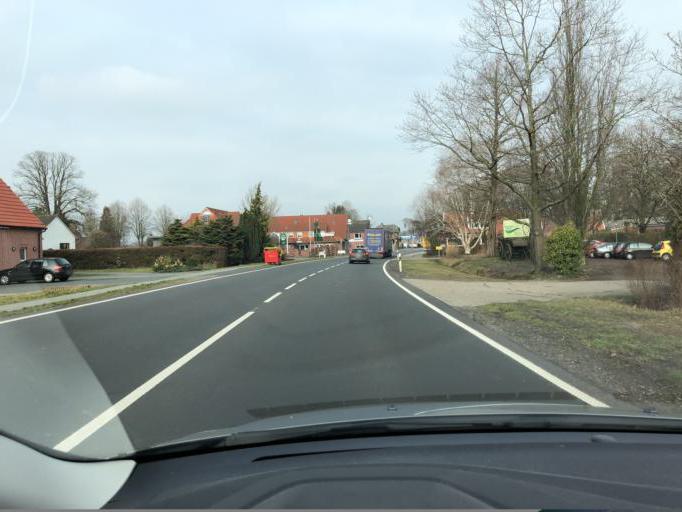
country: DE
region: Lower Saxony
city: Mittegrossefehn
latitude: 53.3944
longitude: 7.5708
